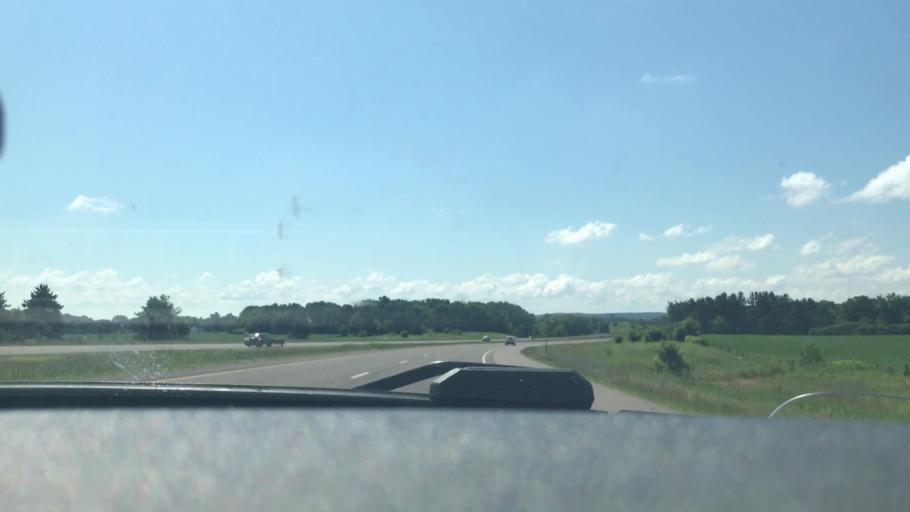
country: US
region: Wisconsin
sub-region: Chippewa County
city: Bloomer
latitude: 45.0234
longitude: -91.4441
